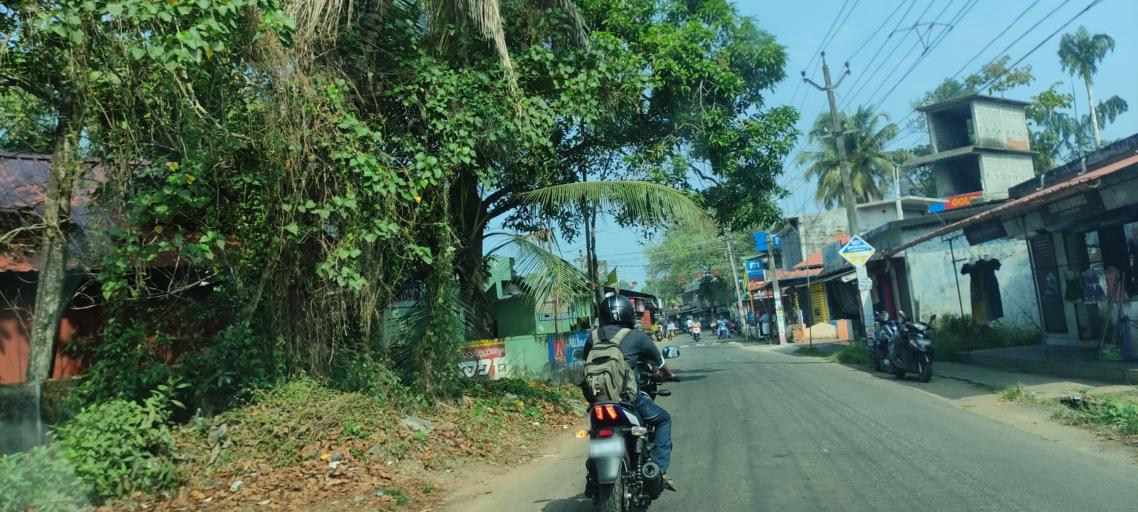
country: IN
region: Kerala
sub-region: Alappuzha
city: Kutiatodu
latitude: 9.7738
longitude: 76.3066
